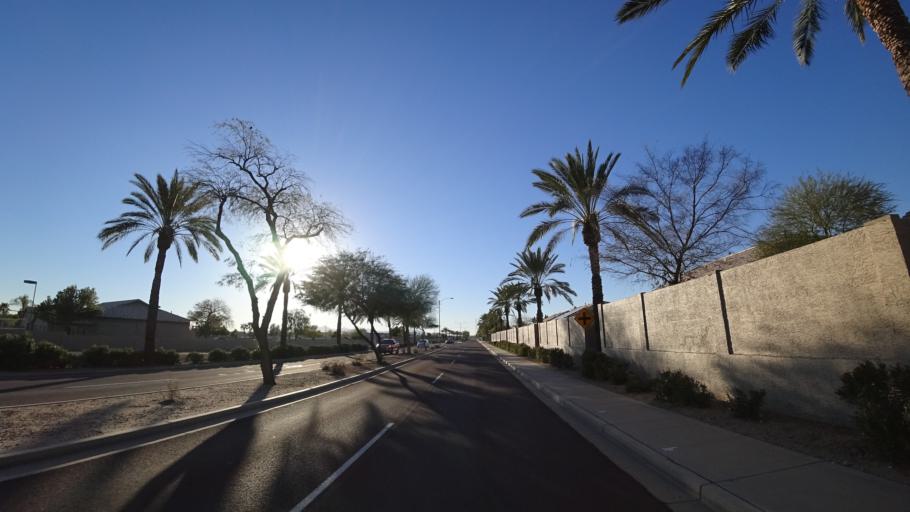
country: US
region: Arizona
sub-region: Maricopa County
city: Sun City West
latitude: 33.6672
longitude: -112.2927
